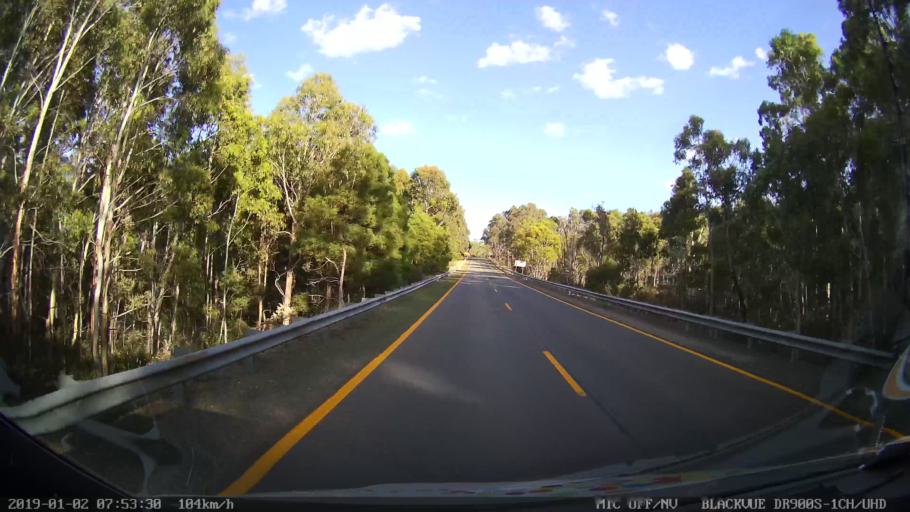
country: AU
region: New South Wales
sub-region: Tumut Shire
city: Tumut
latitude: -35.7045
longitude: 148.5055
